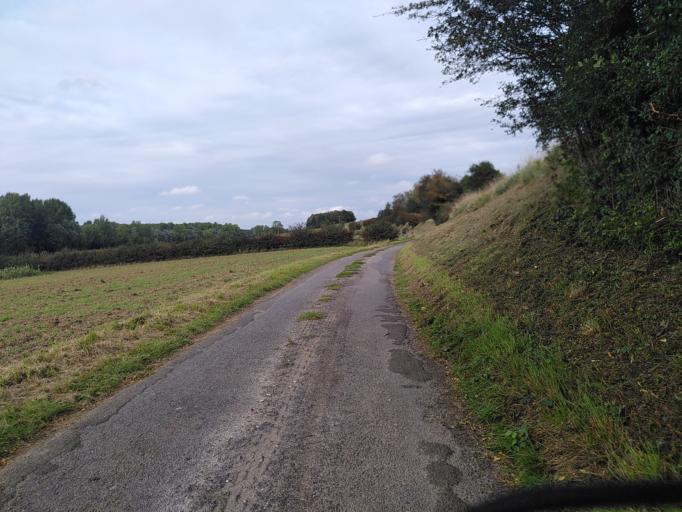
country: FR
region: Nord-Pas-de-Calais
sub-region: Departement du Pas-de-Calais
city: Therouanne
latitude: 50.6073
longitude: 2.1947
